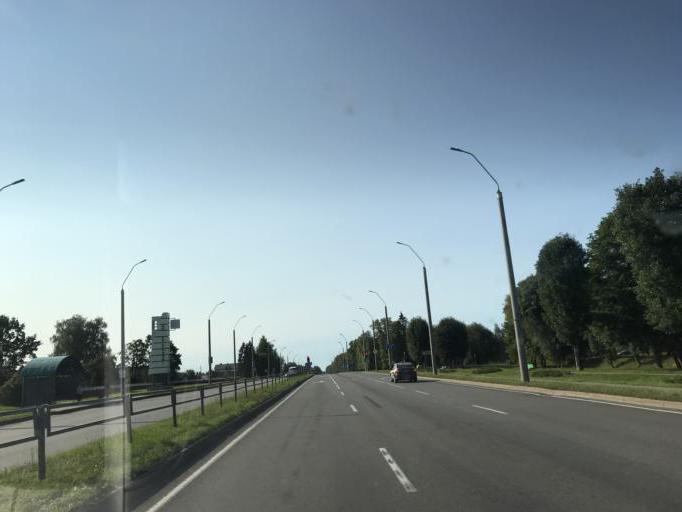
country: BY
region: Mogilev
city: Buynichy
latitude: 53.8609
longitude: 30.2578
